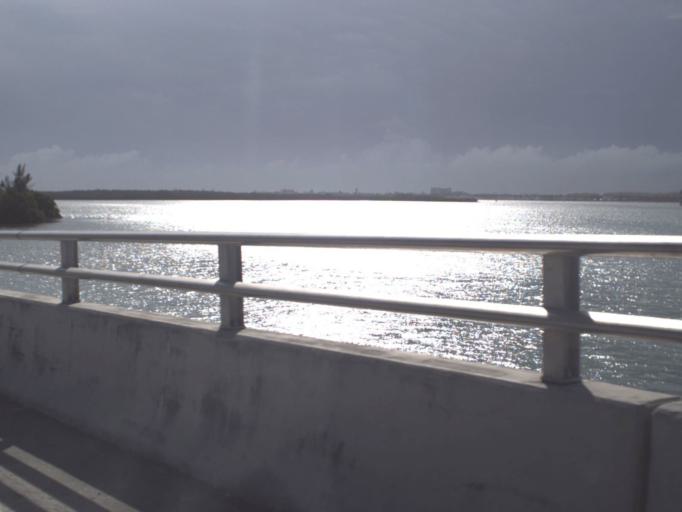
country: US
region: Florida
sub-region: Saint Lucie County
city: Fort Pierce
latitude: 27.4724
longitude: -80.3230
